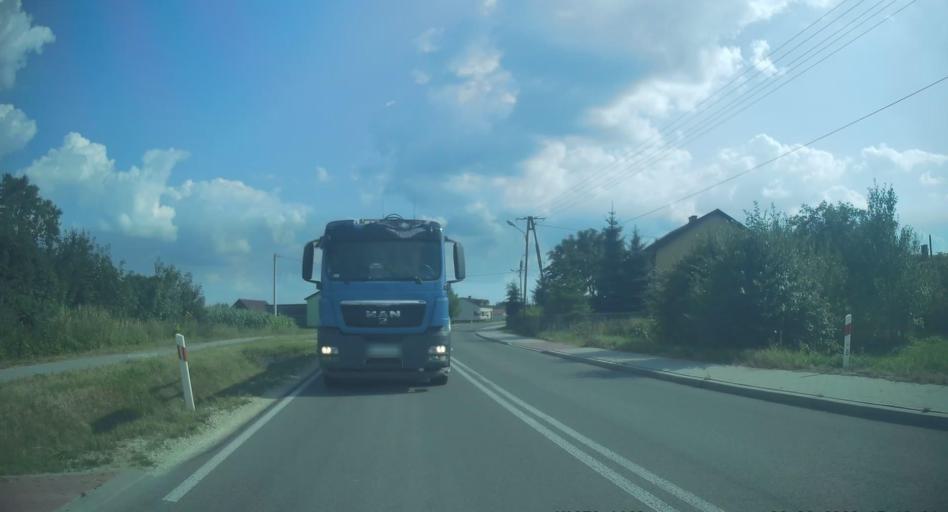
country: PL
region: Swietokrzyskie
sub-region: Powiat konecki
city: Radoszyce
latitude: 51.0467
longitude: 20.2835
